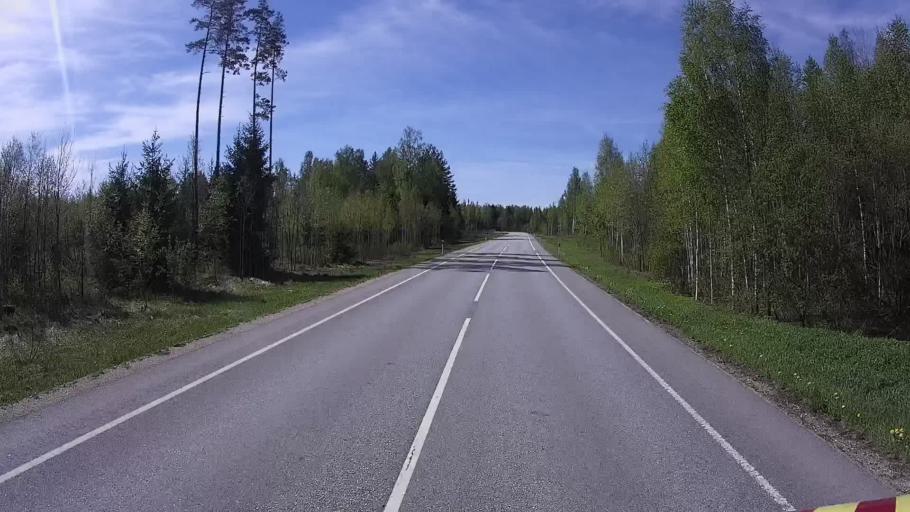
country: RU
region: Pskov
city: Pechory
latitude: 57.8917
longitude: 27.5572
